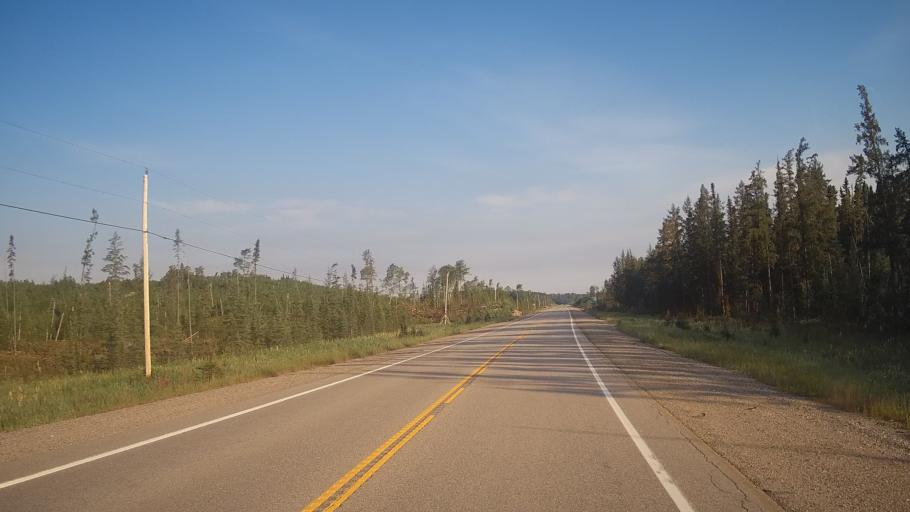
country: CA
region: Ontario
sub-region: Rainy River District
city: Atikokan
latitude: 49.3605
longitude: -91.5413
